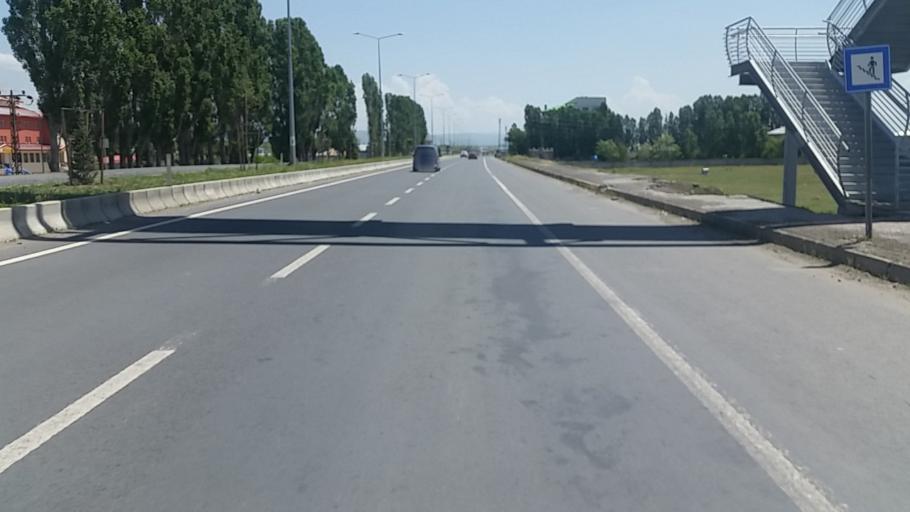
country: TR
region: Agri
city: Agri
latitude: 39.7121
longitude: 43.0835
